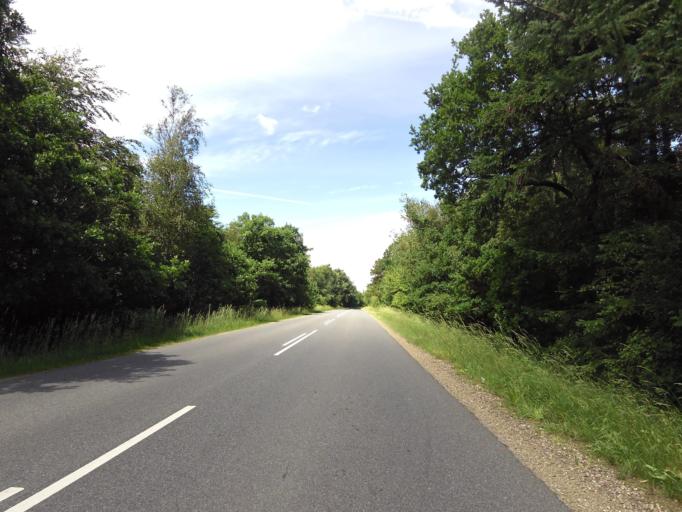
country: DK
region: South Denmark
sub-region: Esbjerg Kommune
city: Ribe
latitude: 55.2992
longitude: 8.7703
